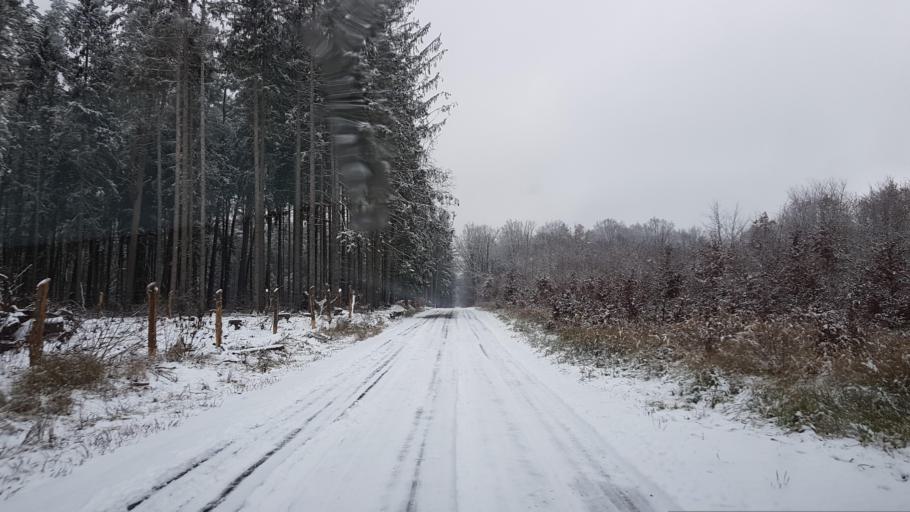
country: PL
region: West Pomeranian Voivodeship
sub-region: Powiat lobeski
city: Resko
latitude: 53.7818
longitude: 15.5318
